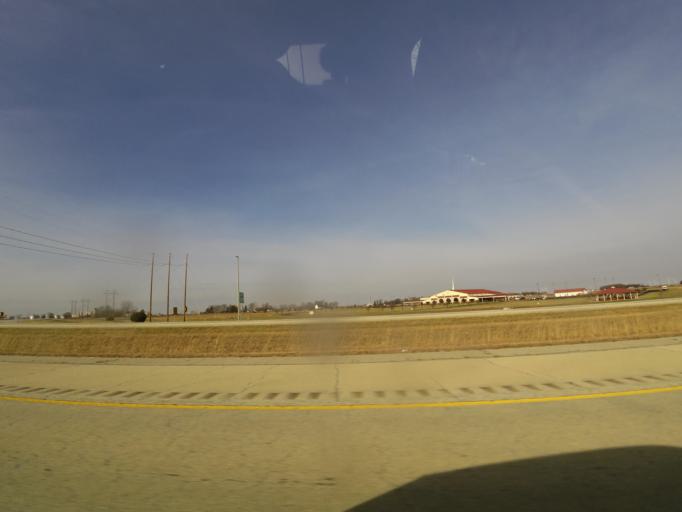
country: US
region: Illinois
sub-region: Macon County
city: Forsyth
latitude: 39.8969
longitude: -89.0028
